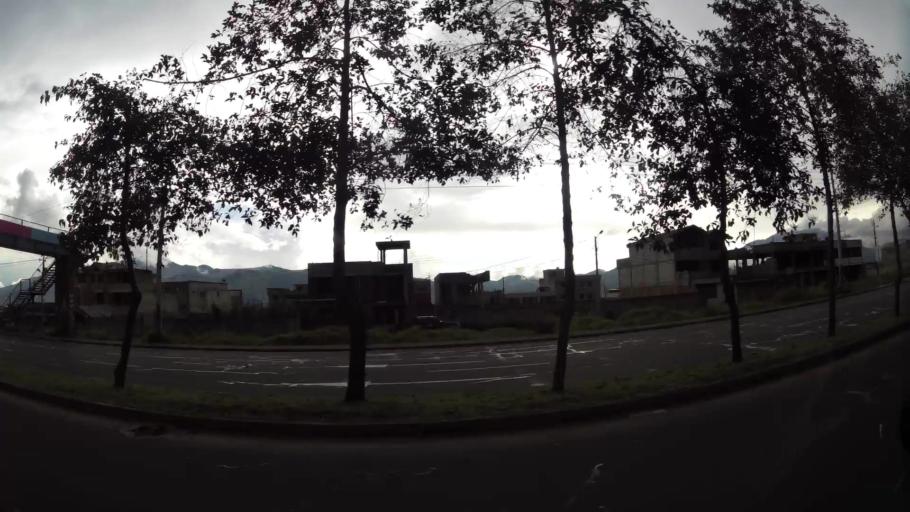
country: EC
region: Pichincha
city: Quito
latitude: -0.2982
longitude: -78.5207
